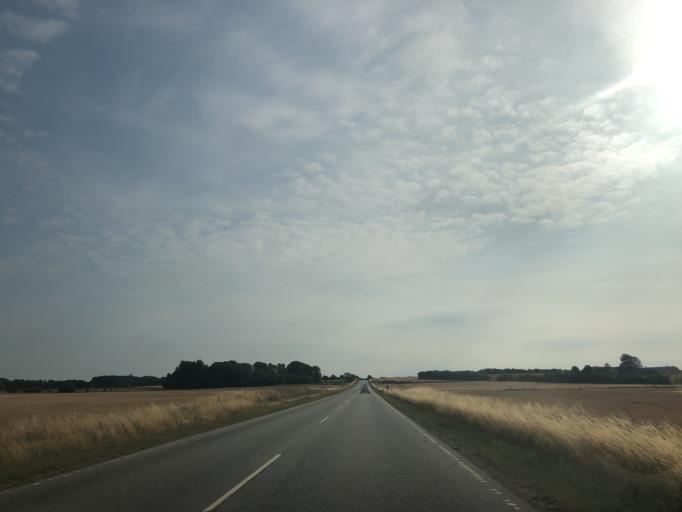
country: DK
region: Central Jutland
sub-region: Skive Kommune
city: Skive
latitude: 56.6672
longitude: 8.9487
